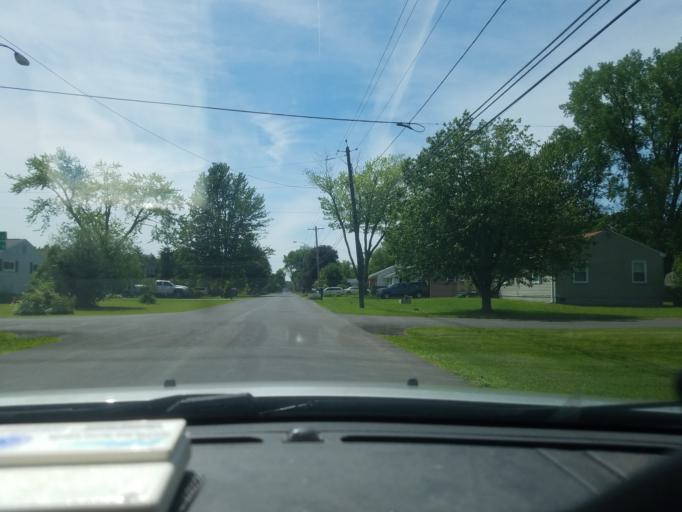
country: US
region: New York
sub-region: Onondaga County
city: East Syracuse
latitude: 43.0828
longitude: -76.0706
